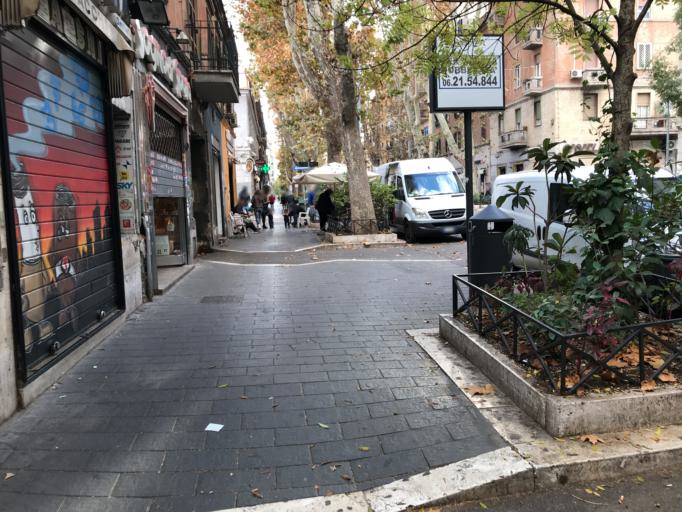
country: IT
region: Latium
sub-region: Citta metropolitana di Roma Capitale
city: Rome
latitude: 41.8795
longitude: 12.5420
